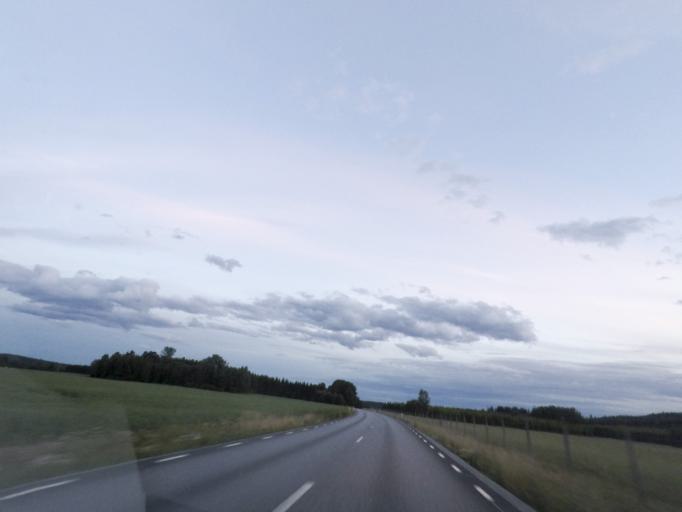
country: SE
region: Uppsala
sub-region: Habo Kommun
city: Balsta
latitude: 59.6397
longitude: 17.5260
